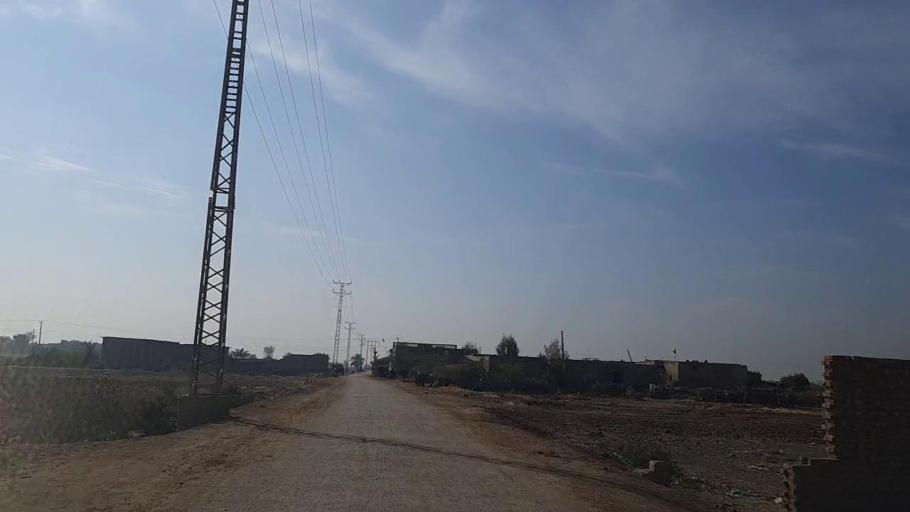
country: PK
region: Sindh
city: Mirpur Khas
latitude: 25.5035
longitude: 69.0000
